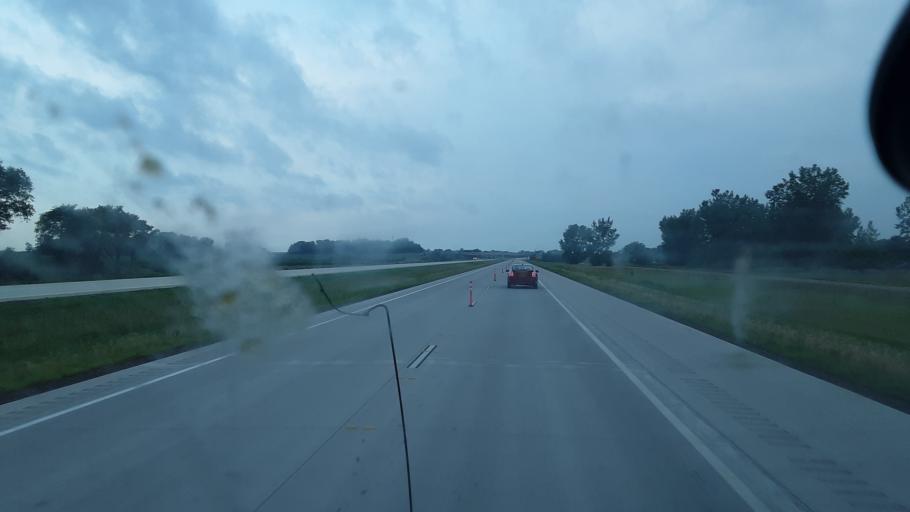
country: US
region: Minnesota
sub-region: Martin County
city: Fairmont
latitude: 43.6707
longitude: -94.3972
